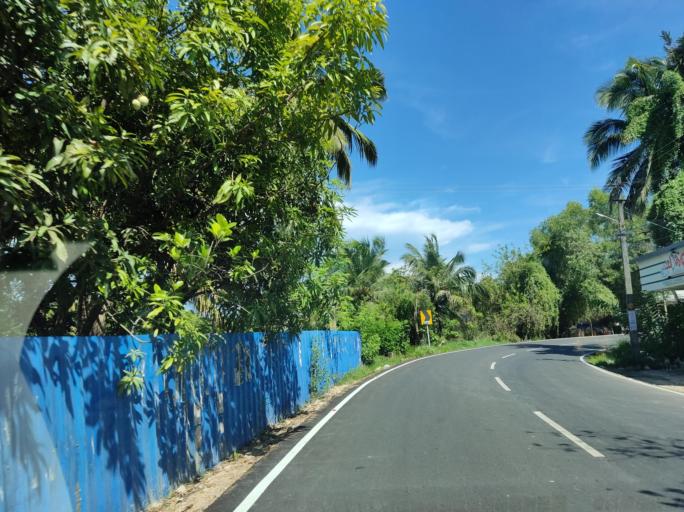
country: IN
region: Kerala
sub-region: Alappuzha
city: Kayankulam
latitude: 9.1703
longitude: 76.4597
